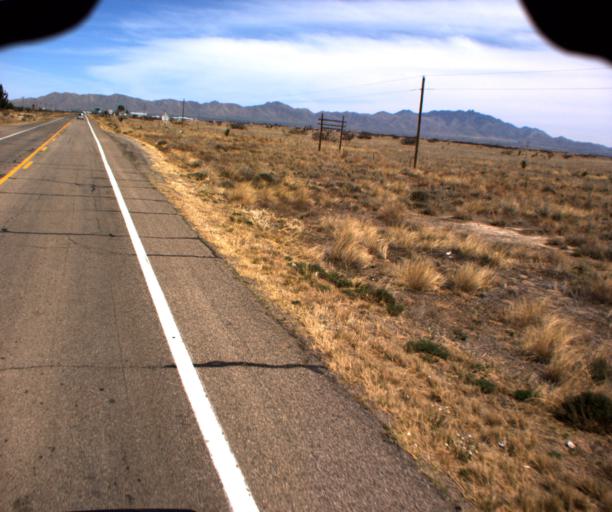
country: US
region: Arizona
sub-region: Cochise County
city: Willcox
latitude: 32.2218
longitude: -109.8736
